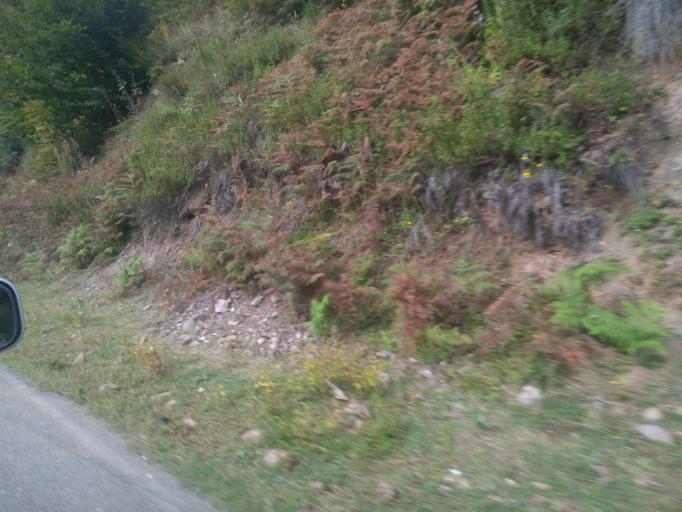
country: TR
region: Artvin
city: Camili
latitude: 41.5593
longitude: 41.8179
